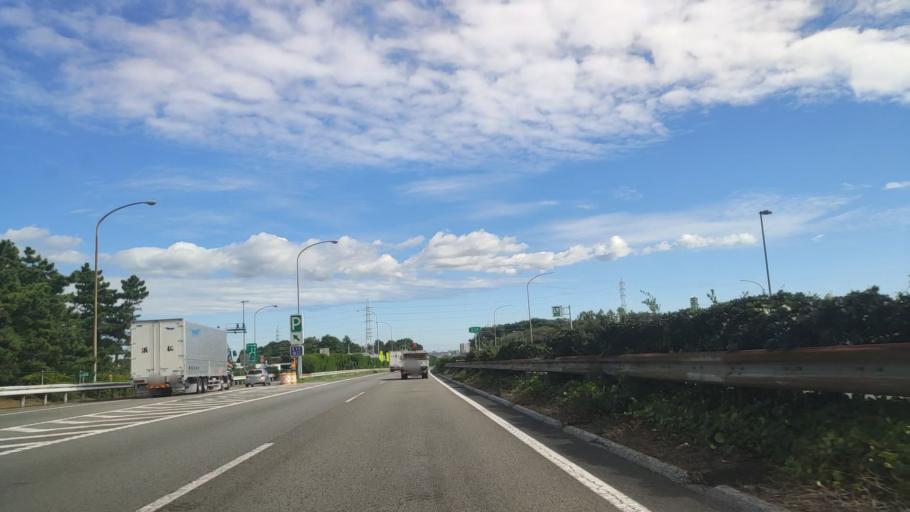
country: JP
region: Shizuoka
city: Hamamatsu
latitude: 34.7585
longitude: 137.7362
